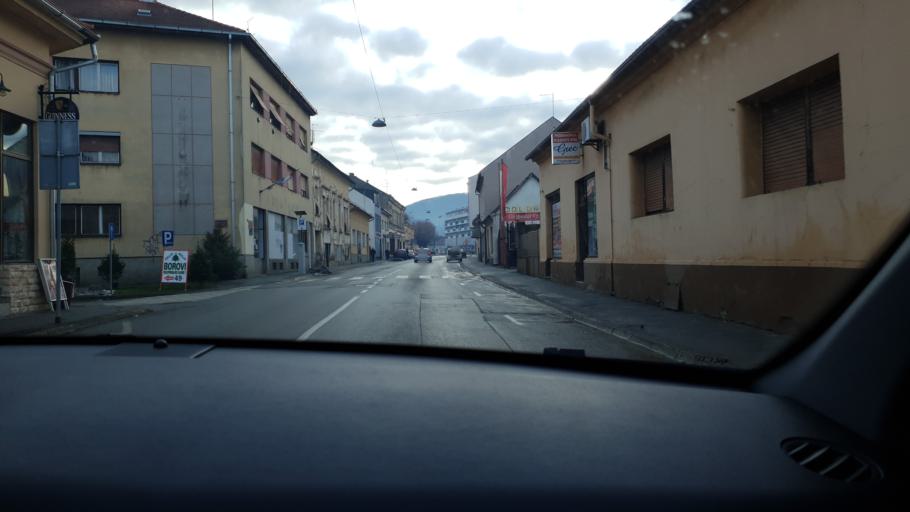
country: HR
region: Pozesko-Slavonska
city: Pozega
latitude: 45.3365
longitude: 17.6794
